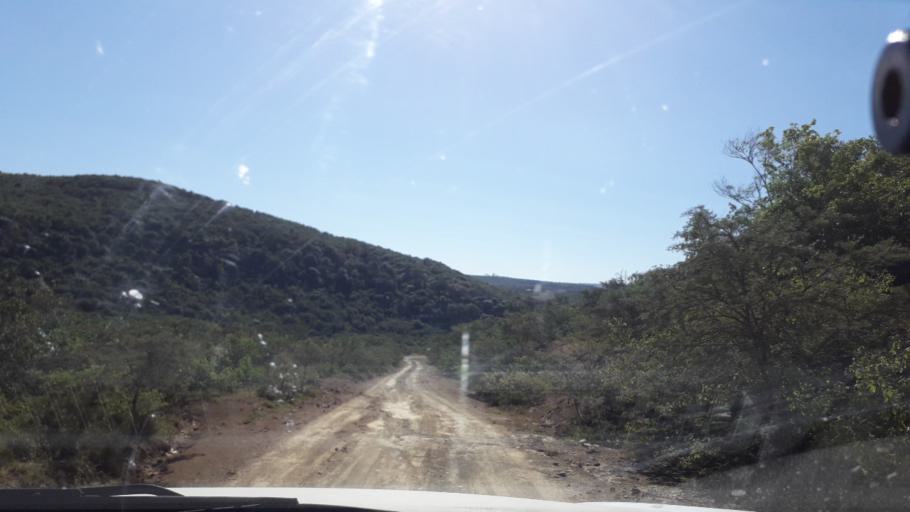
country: ZA
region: Eastern Cape
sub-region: Amathole District Municipality
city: Komga
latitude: -32.7722
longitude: 27.9606
